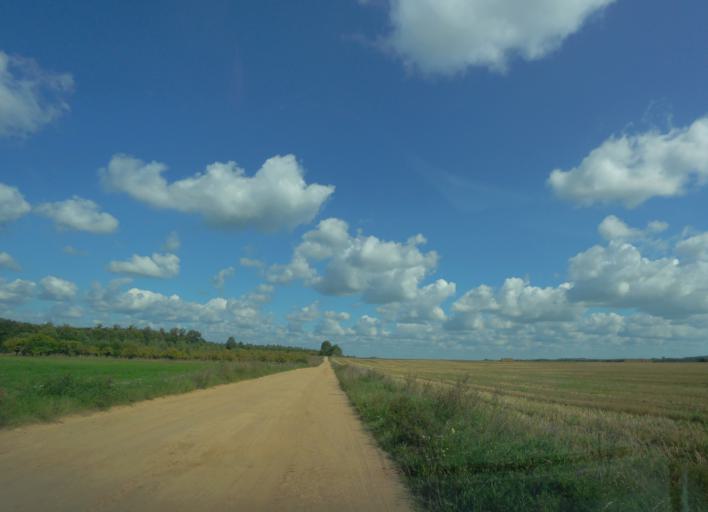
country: BY
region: Minsk
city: Zyembin
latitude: 54.3759
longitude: 28.3453
